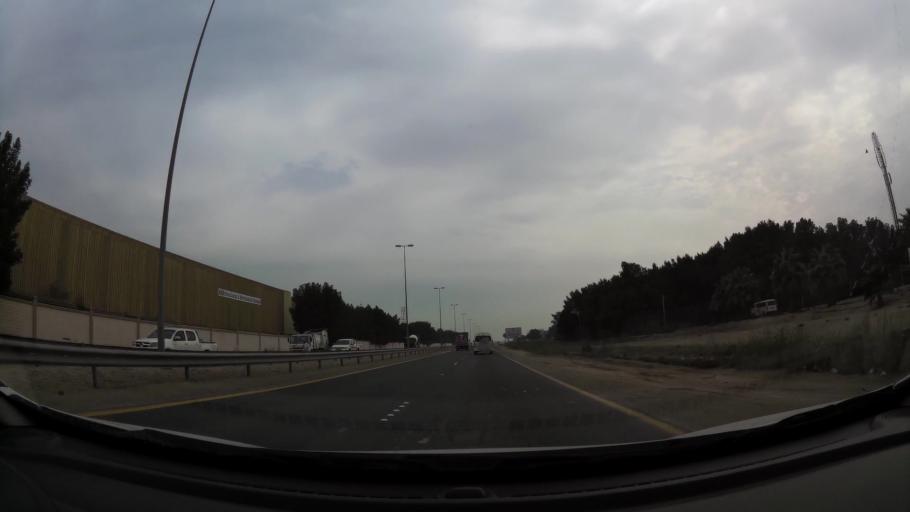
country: BH
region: Northern
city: Sitrah
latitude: 26.0834
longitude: 50.6125
